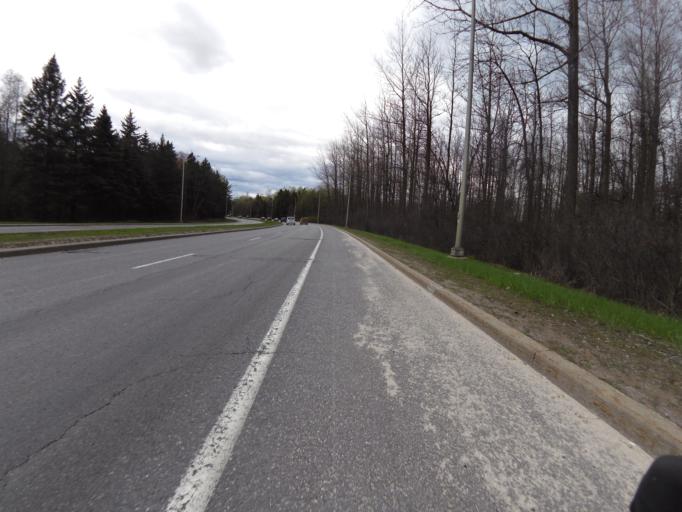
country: CA
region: Ontario
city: Ottawa
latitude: 45.3328
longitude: -75.7338
